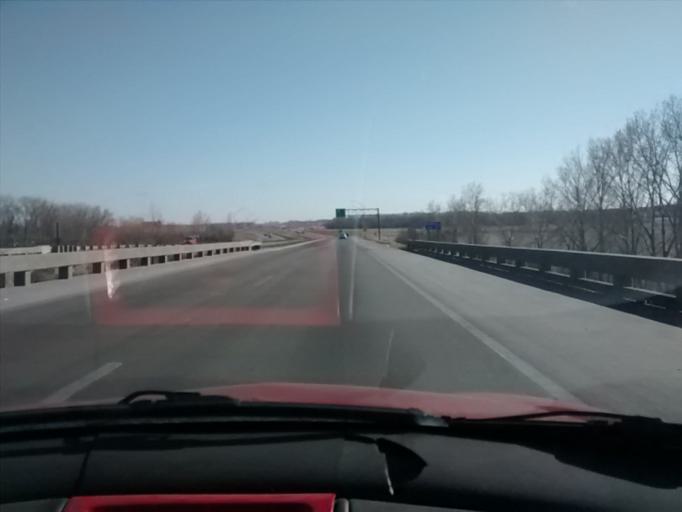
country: US
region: Nebraska
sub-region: Sarpy County
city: Offutt Air Force Base
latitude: 41.1479
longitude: -95.9389
